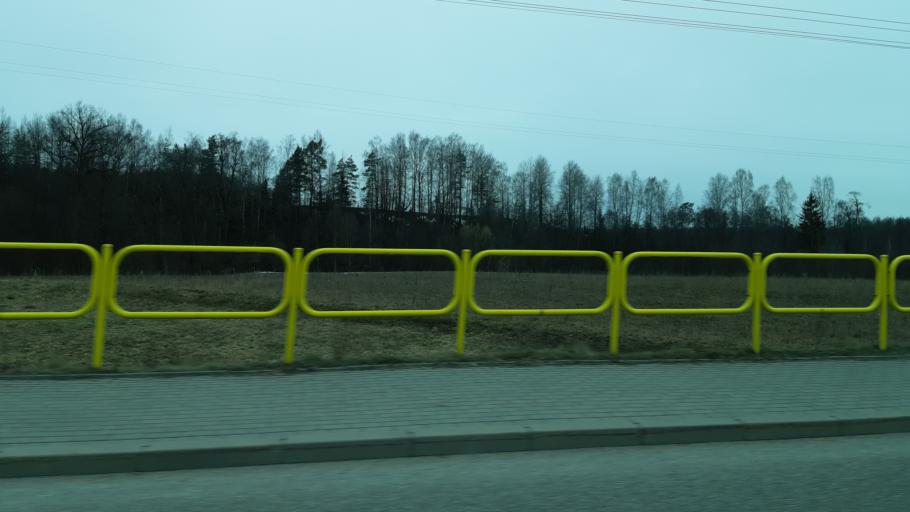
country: PL
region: Podlasie
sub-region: Suwalki
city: Suwalki
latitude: 54.3193
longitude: 22.9649
